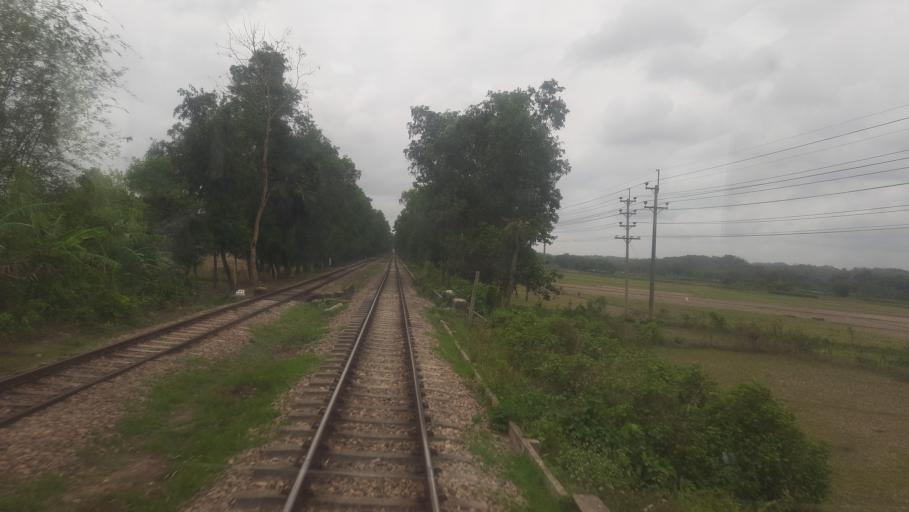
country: BD
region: Chittagong
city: Fatikchari
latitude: 22.7711
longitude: 91.5899
